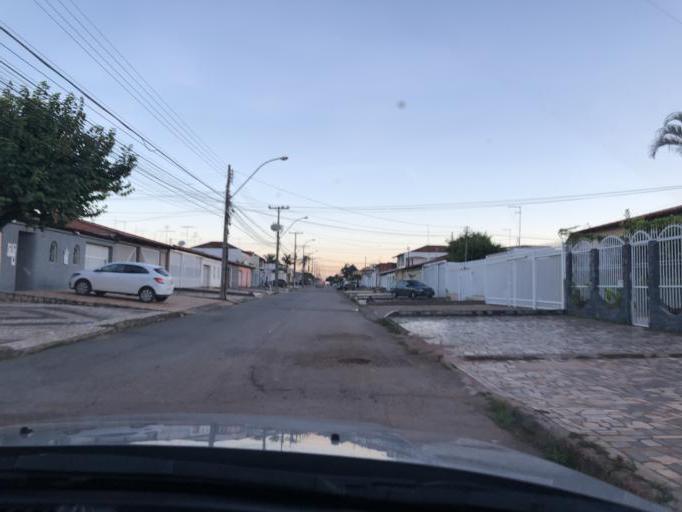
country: BR
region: Federal District
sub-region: Brasilia
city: Brasilia
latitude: -15.8043
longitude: -48.0689
